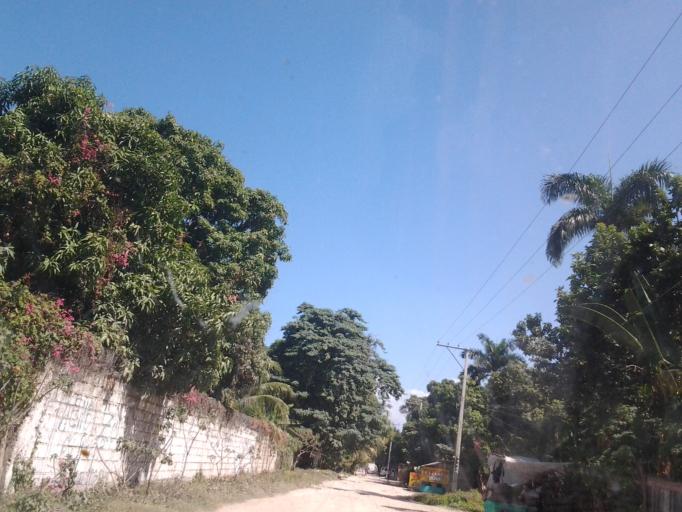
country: HT
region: Ouest
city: Grangwav
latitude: 18.4261
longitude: -72.7753
